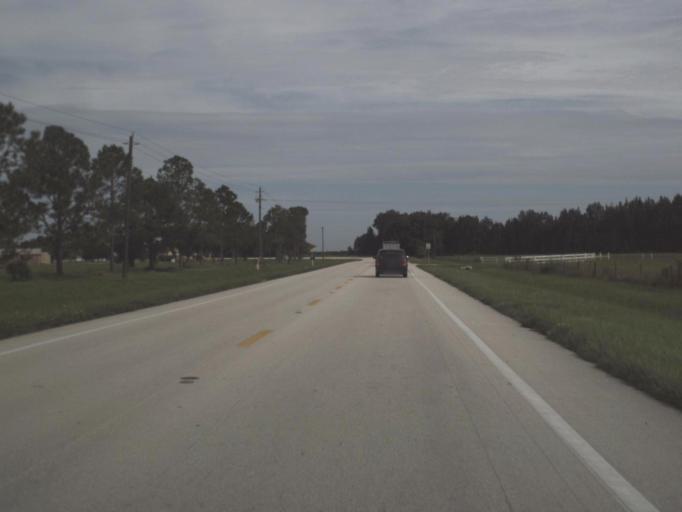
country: US
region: Florida
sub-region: DeSoto County
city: Southeast Arcadia
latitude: 27.1344
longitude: -81.7961
